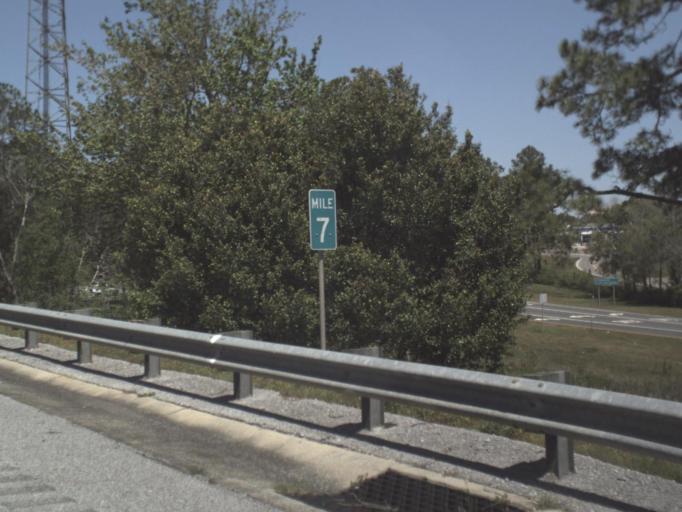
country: US
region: Florida
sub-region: Escambia County
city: Ensley
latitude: 30.5210
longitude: -87.3125
